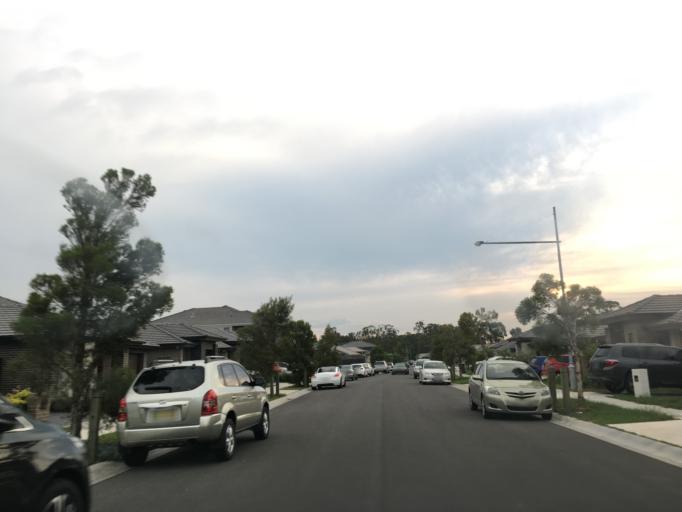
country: AU
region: New South Wales
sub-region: Campbelltown Municipality
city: Denham Court
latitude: -33.9796
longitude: 150.8051
